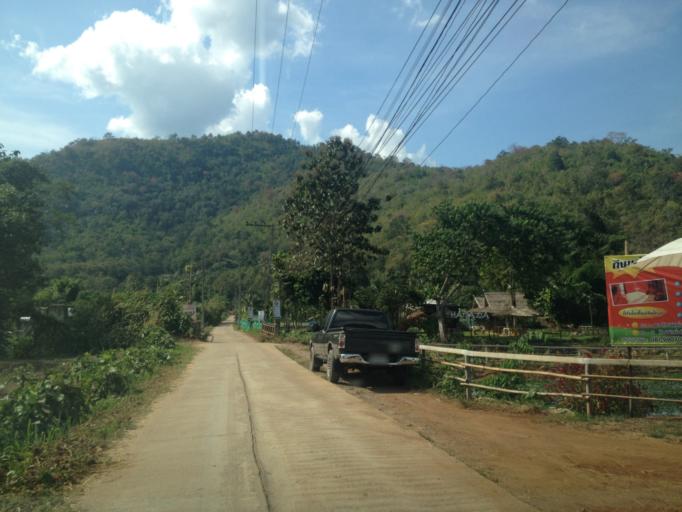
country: TH
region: Chiang Mai
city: Samoeng
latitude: 18.8400
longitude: 98.7305
